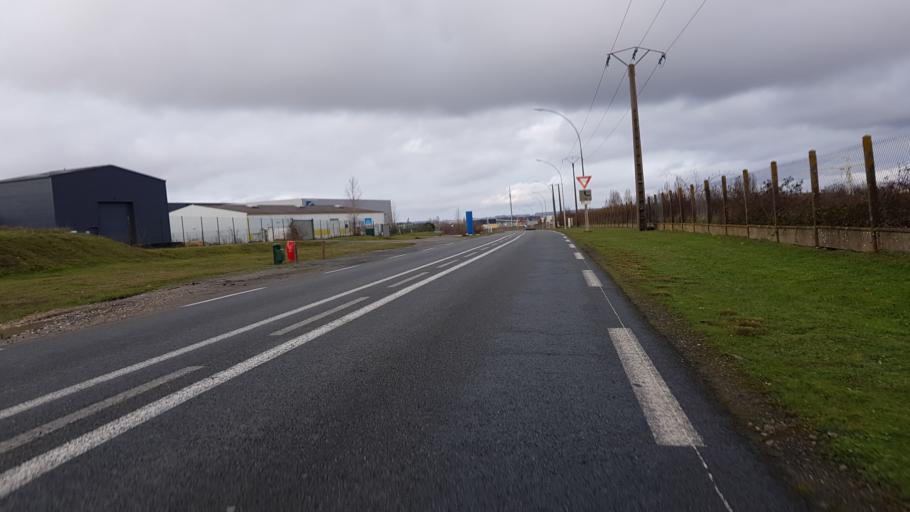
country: FR
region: Poitou-Charentes
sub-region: Departement de la Vienne
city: Chasseneuil-du-Poitou
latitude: 46.6618
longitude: 0.3761
